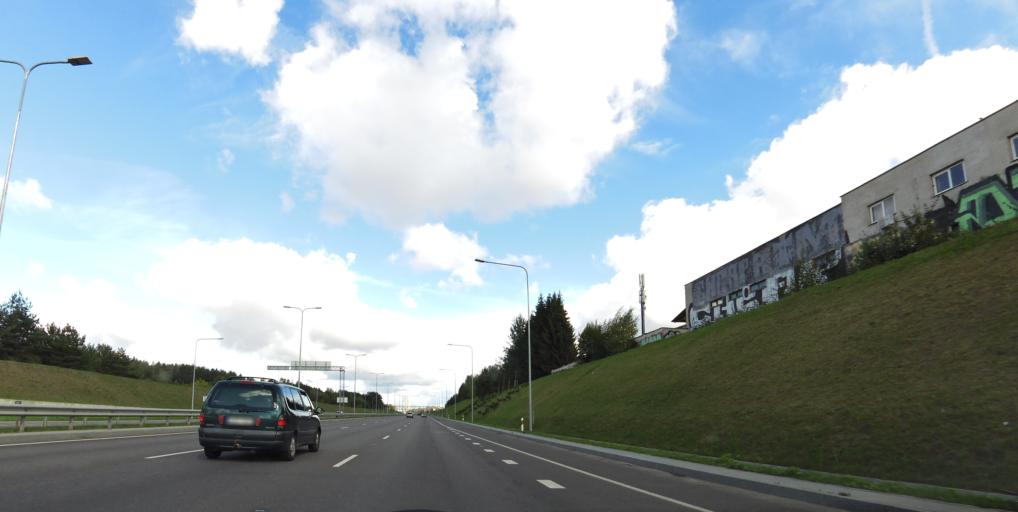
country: LT
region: Vilnius County
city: Pilaite
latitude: 54.6861
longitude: 25.1968
